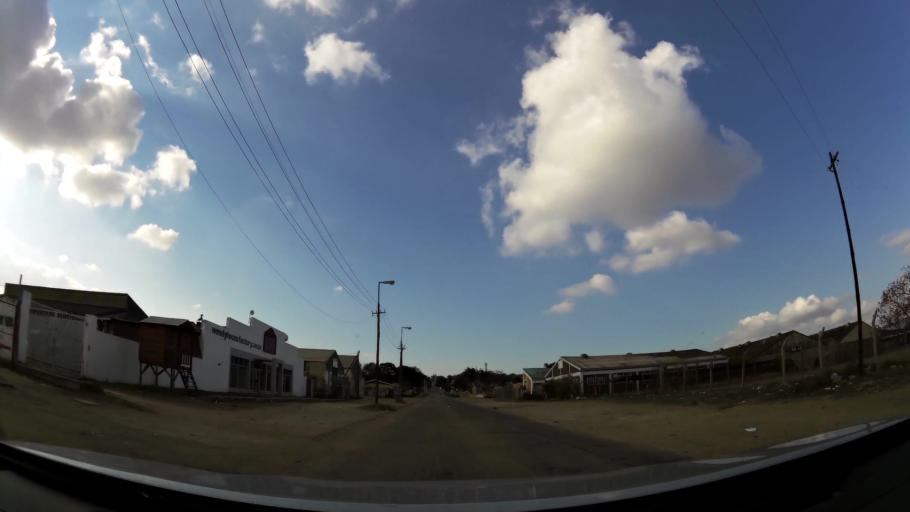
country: ZA
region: Eastern Cape
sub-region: Nelson Mandela Bay Metropolitan Municipality
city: Uitenhage
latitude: -33.7727
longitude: 25.3928
